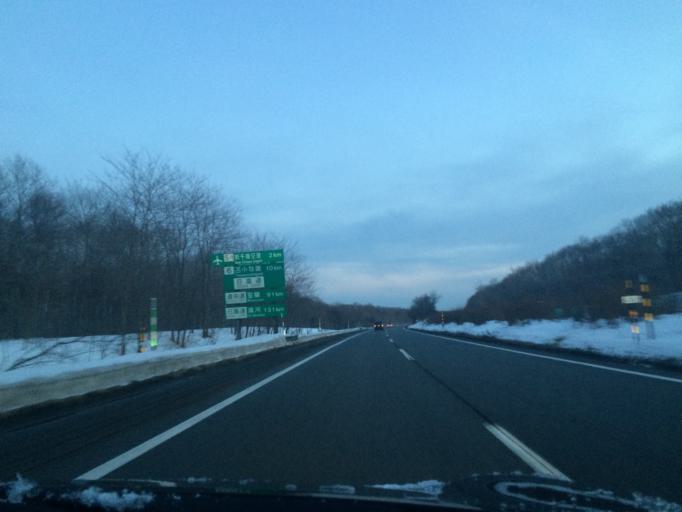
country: JP
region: Hokkaido
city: Chitose
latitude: 42.8004
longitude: 141.6259
